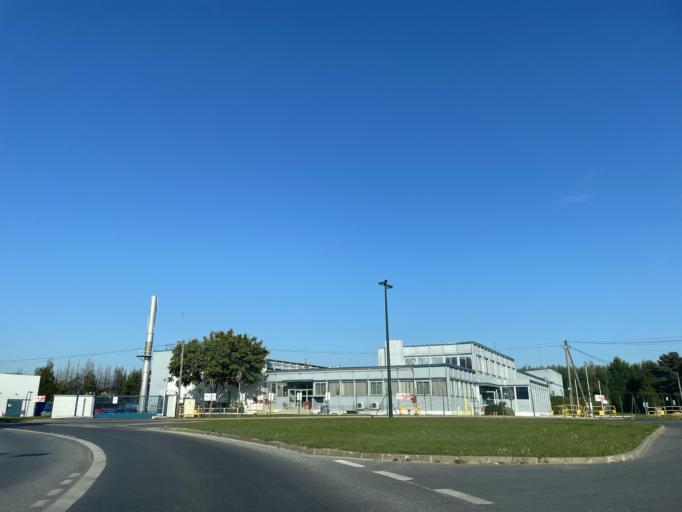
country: FR
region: Ile-de-France
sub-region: Departement de Seine-et-Marne
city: Coulommiers
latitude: 48.8063
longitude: 3.0938
